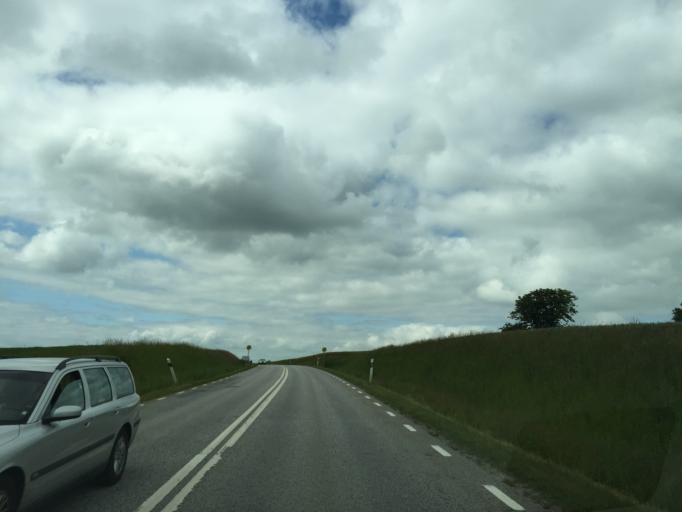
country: SE
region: Skane
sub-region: Svedala Kommun
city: Klagerup
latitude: 55.6207
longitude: 13.2581
